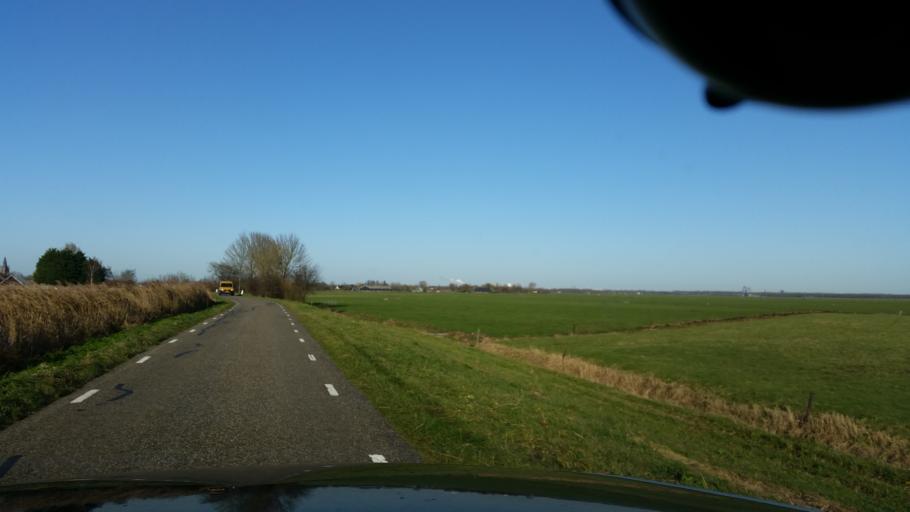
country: NL
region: North Holland
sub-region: Gemeente Ouder-Amstel
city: Ouderkerk aan de Amstel
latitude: 52.2521
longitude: 4.8854
